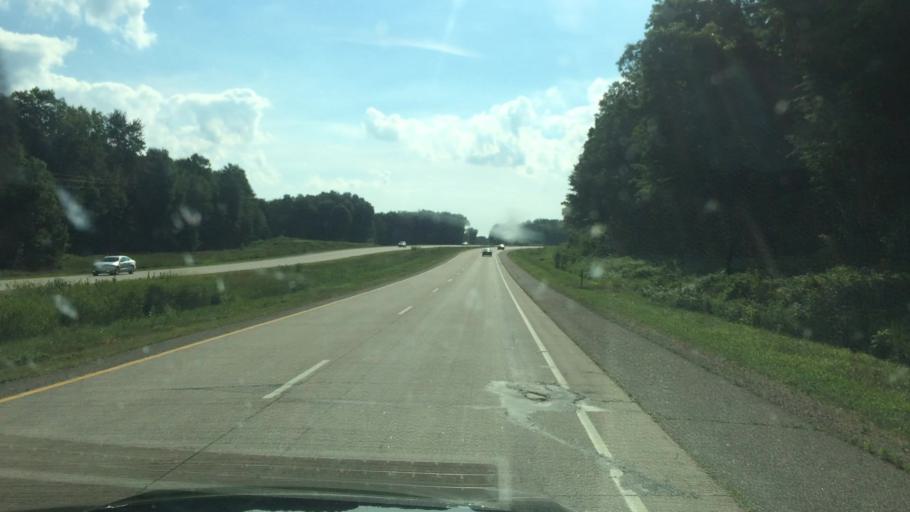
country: US
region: Wisconsin
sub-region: Shawano County
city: Wittenberg
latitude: 44.8258
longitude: -89.0730
